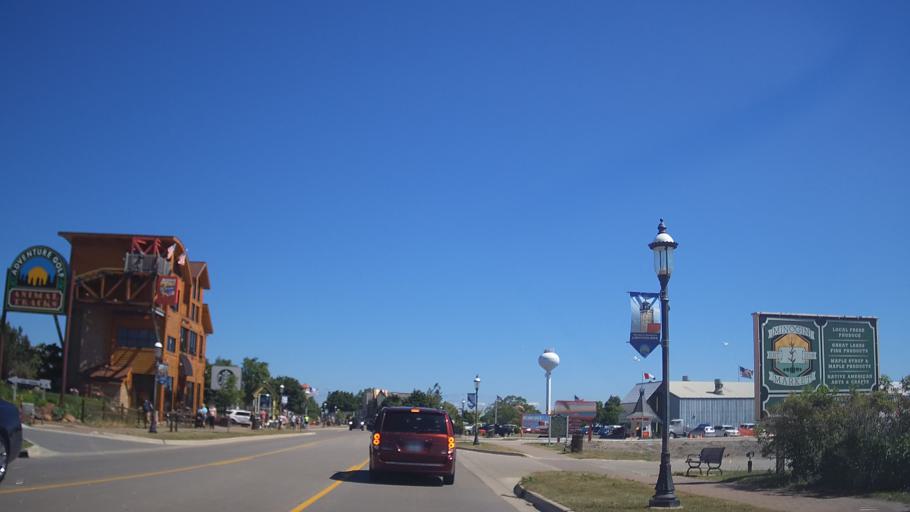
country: US
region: Michigan
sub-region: Mackinac County
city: Saint Ignace
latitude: 45.7791
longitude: -84.7260
